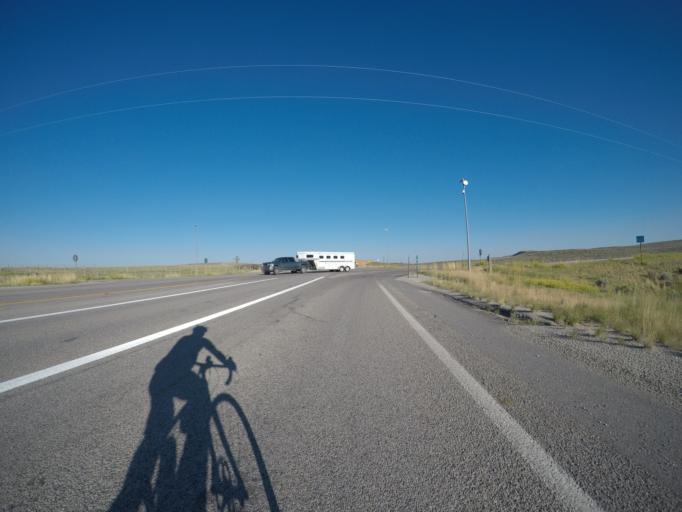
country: US
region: Wyoming
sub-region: Sublette County
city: Pinedale
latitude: 42.8809
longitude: -109.9742
